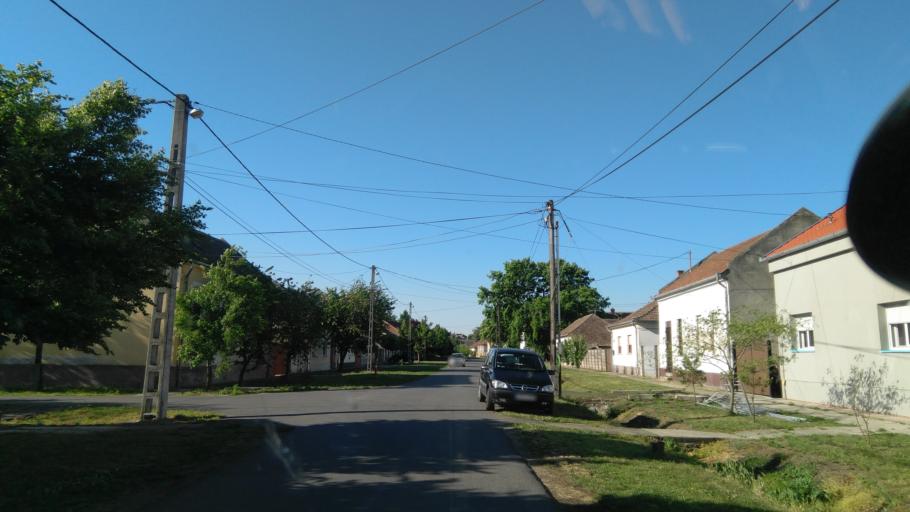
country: HU
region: Bekes
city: Elek
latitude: 46.5315
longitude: 21.2561
